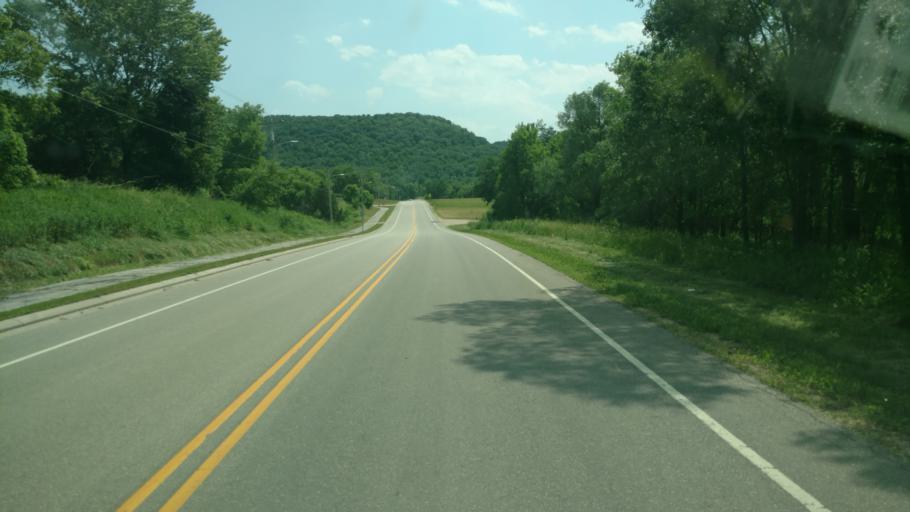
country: US
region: Wisconsin
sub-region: Vernon County
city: Viroqua
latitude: 43.4972
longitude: -90.6802
